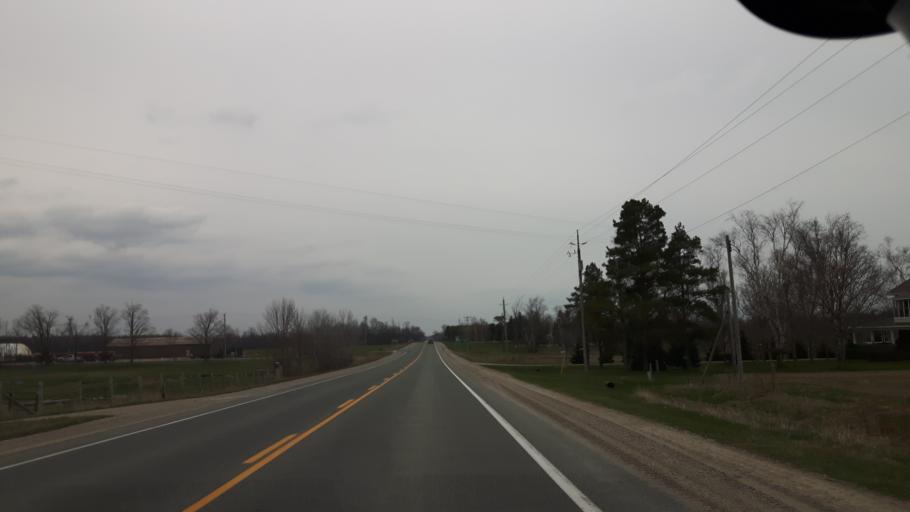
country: CA
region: Ontario
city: Goderich
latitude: 43.6073
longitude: -81.7057
